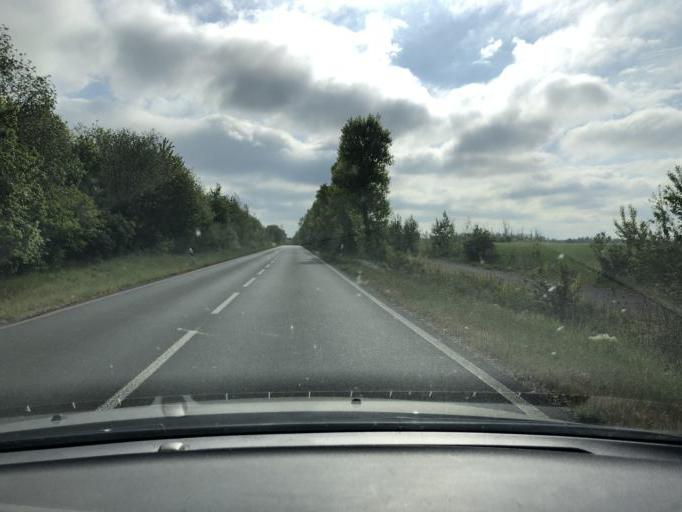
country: DE
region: Saxony
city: Neukieritzsch
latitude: 51.1538
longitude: 12.4293
